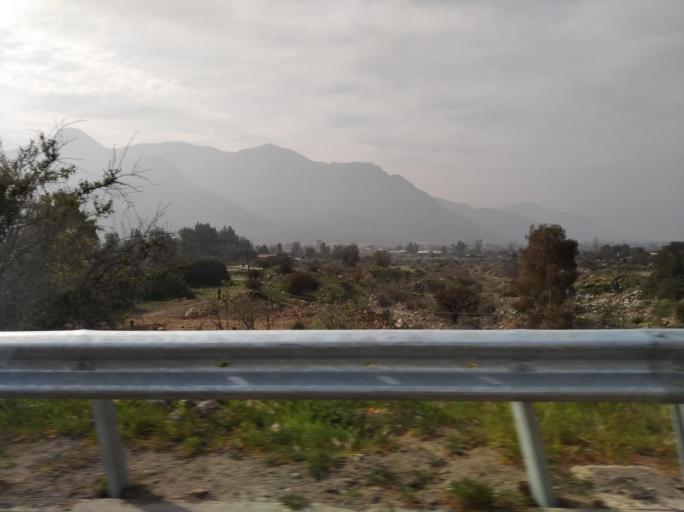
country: CL
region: Santiago Metropolitan
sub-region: Provincia de Chacabuco
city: Lampa
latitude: -33.2361
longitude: -70.9258
